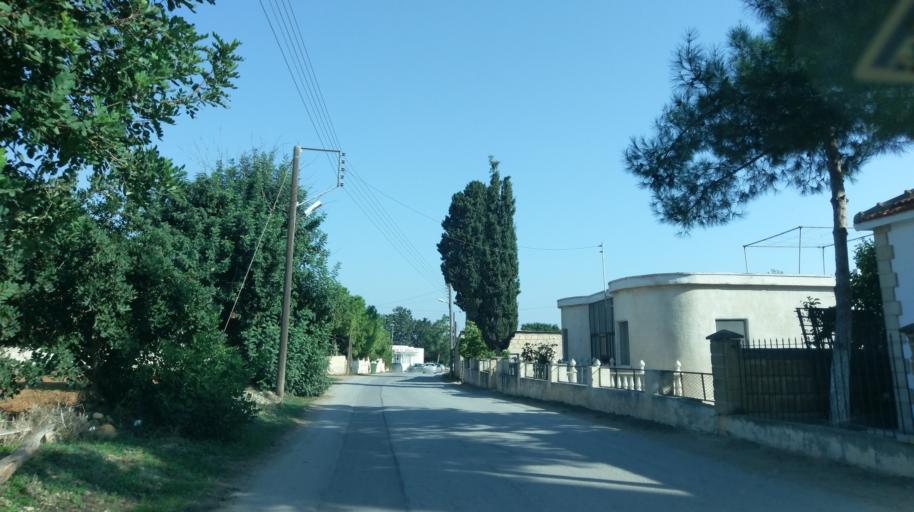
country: CY
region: Ammochostos
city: Leonarisso
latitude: 35.4723
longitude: 34.1496
